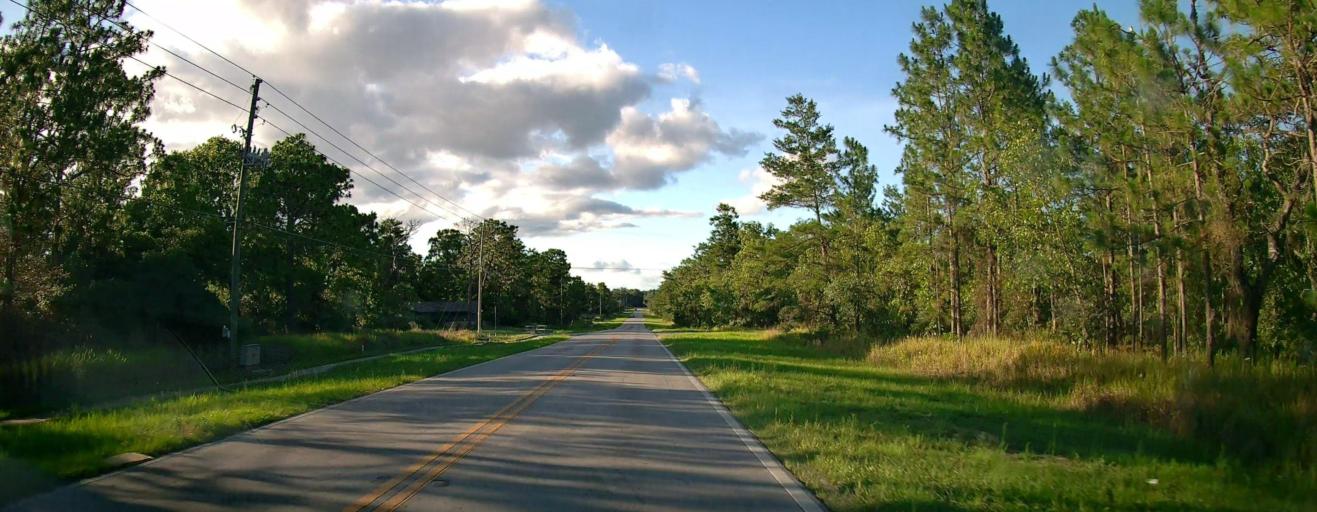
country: US
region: Florida
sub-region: Marion County
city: Silver Springs Shores
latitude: 29.0702
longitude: -82.0078
